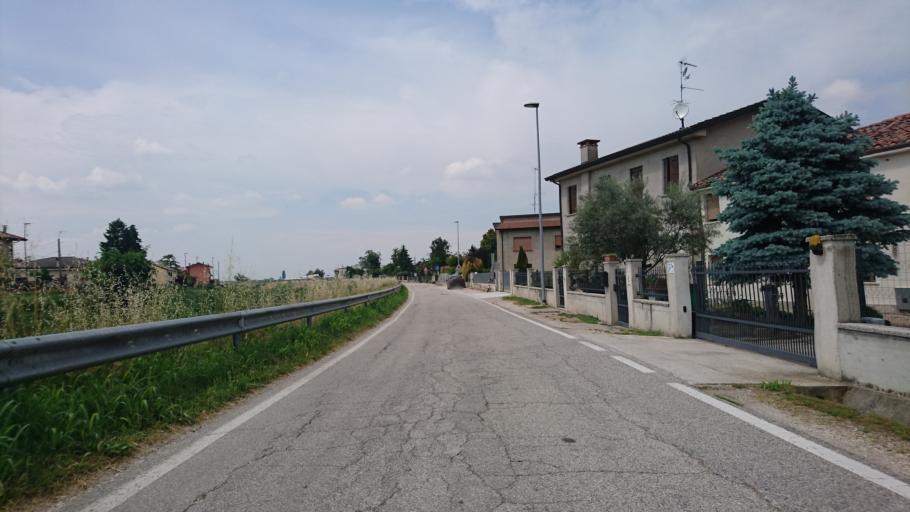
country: IT
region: Veneto
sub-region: Provincia di Rovigo
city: Giacciano con Baruchella
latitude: 45.0675
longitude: 11.4517
